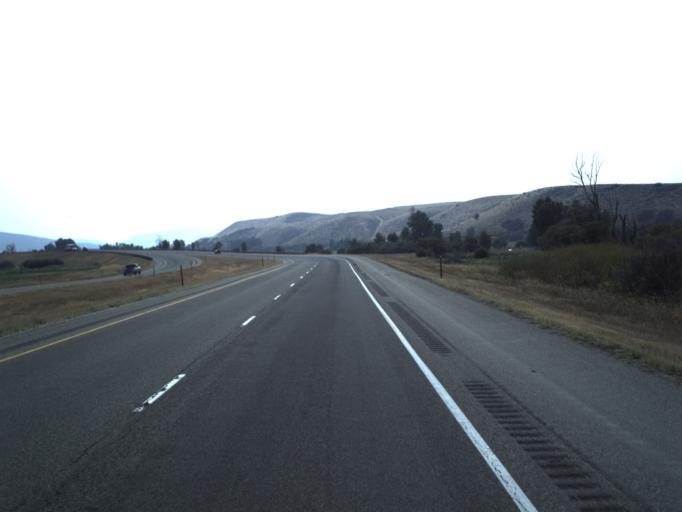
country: US
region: Utah
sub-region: Summit County
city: Coalville
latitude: 40.8535
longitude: -111.3885
